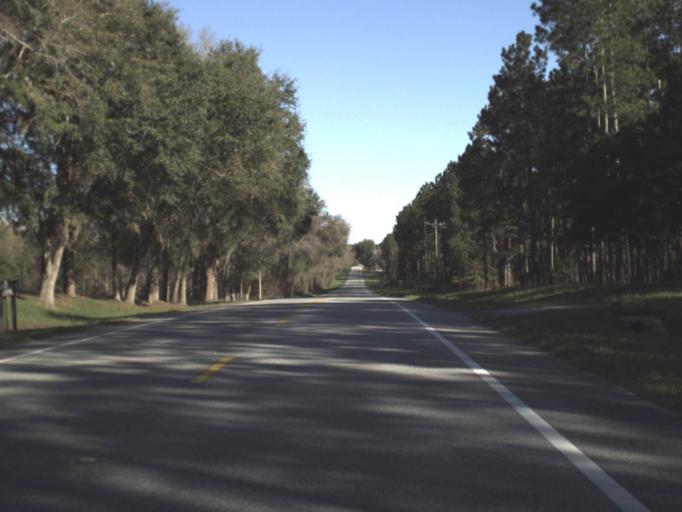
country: US
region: Georgia
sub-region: Brooks County
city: Quitman
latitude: 30.5989
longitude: -83.6432
